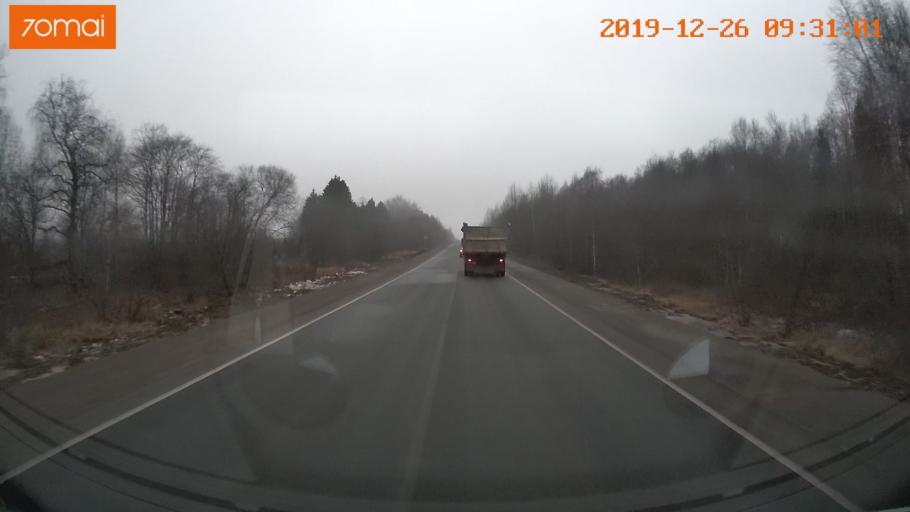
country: RU
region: Vologda
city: Gryazovets
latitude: 59.0656
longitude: 40.1326
